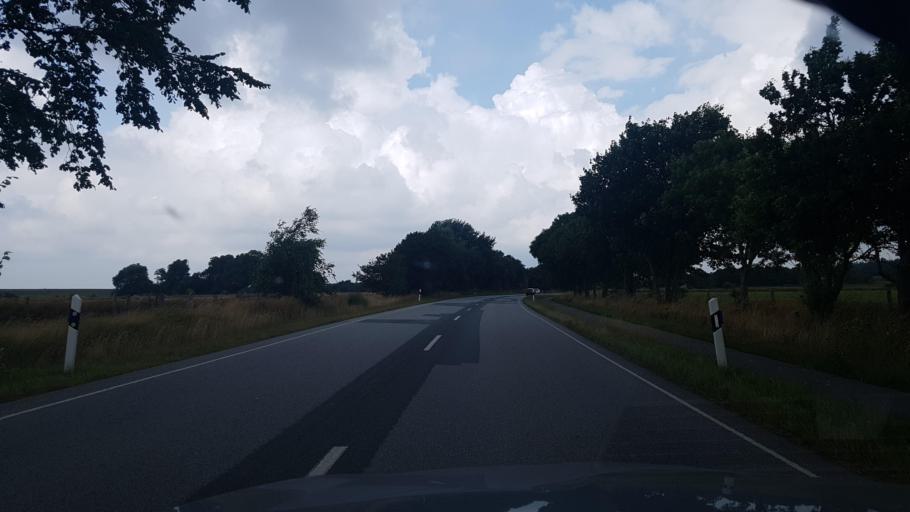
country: DE
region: Schleswig-Holstein
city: Schobull
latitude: 54.4979
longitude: 9.0233
